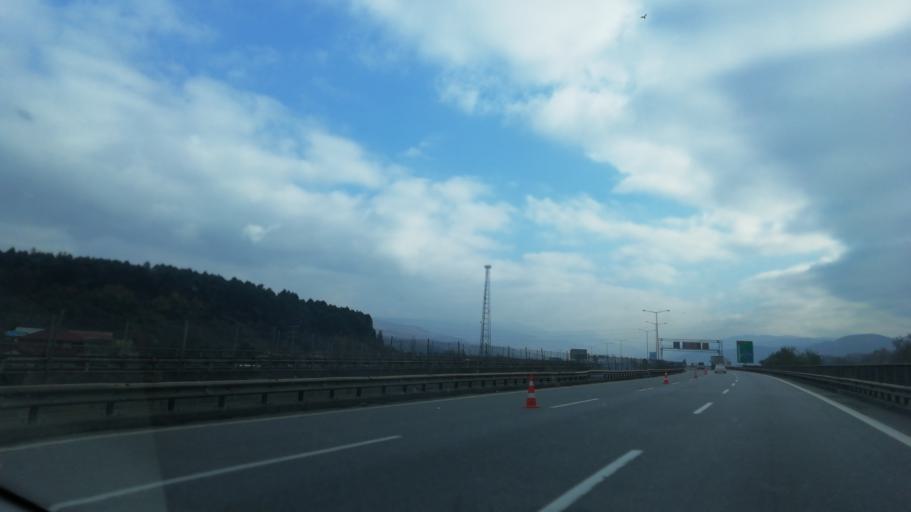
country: TR
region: Duzce
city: Kaynasli
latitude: 40.7862
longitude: 31.2623
